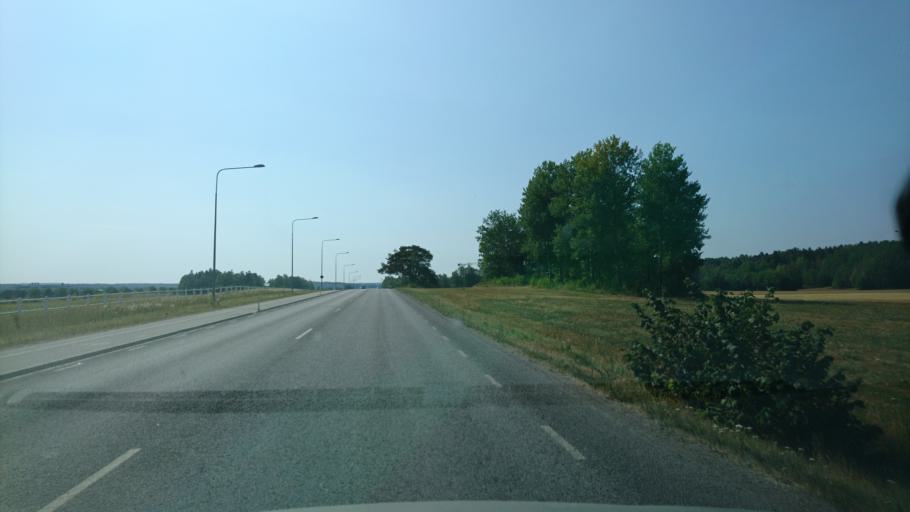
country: SE
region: Uppsala
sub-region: Uppsala Kommun
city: Uppsala
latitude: 59.8220
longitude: 17.6464
